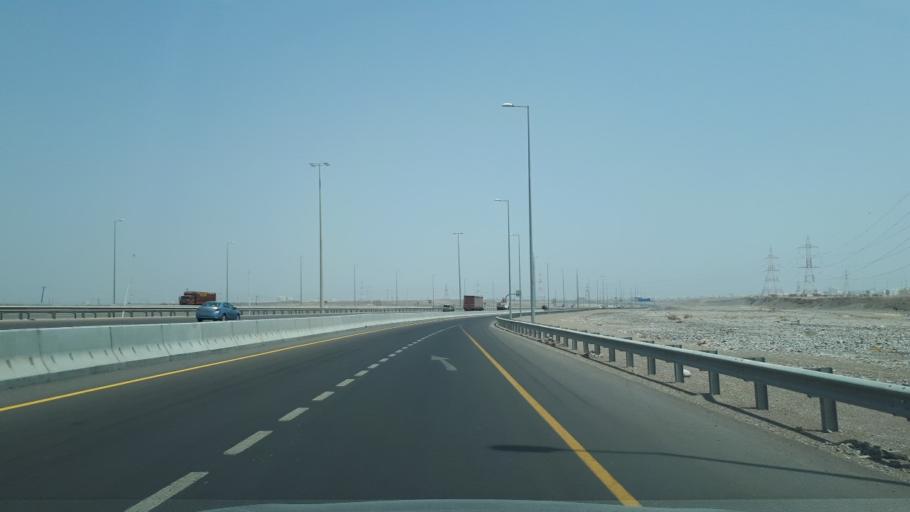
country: OM
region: Muhafazat Masqat
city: As Sib al Jadidah
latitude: 23.6113
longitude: 58.0907
